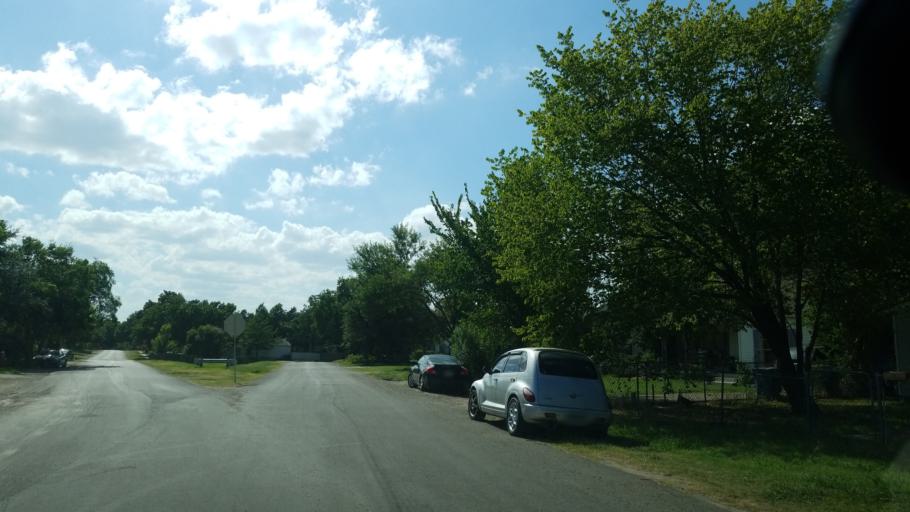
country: US
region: Texas
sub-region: Dallas County
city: Balch Springs
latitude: 32.7701
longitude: -96.7034
